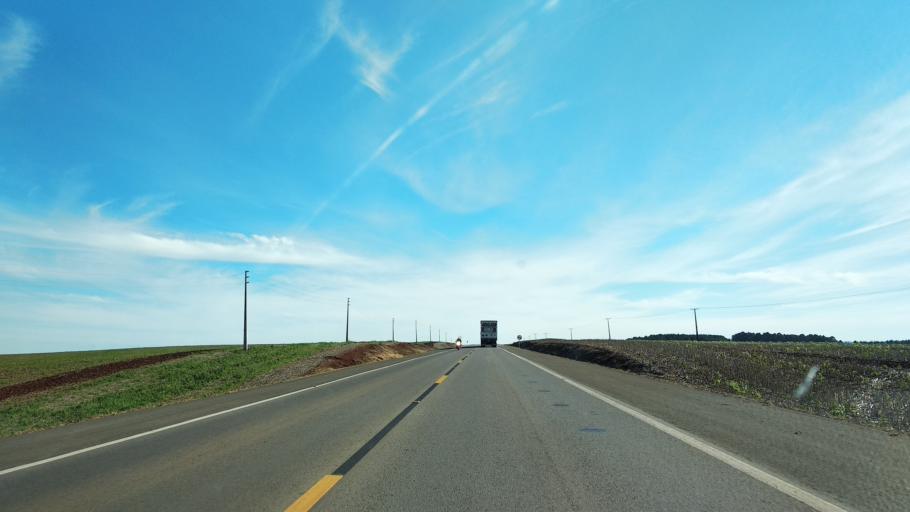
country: BR
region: Santa Catarina
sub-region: Campos Novos
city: Campos Novos
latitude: -27.4875
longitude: -51.3218
